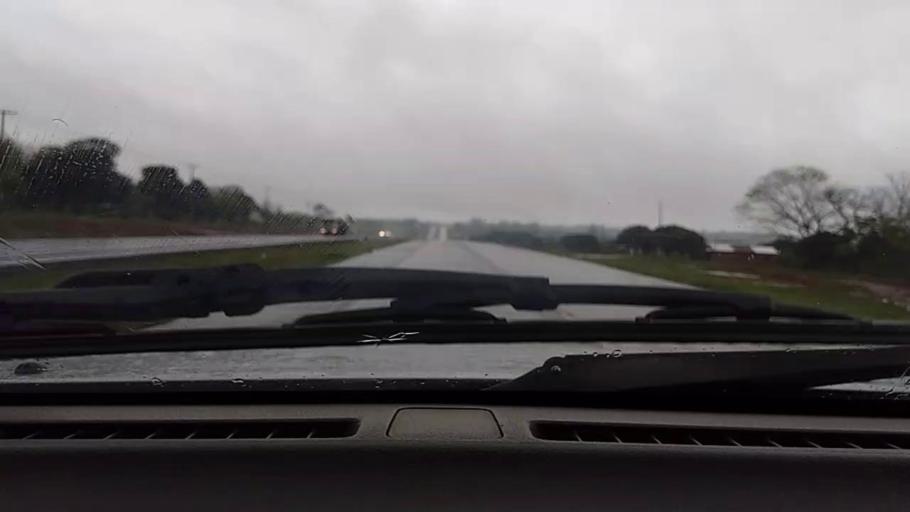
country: PY
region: Caaguazu
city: Repatriacion
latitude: -25.4660
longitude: -55.9486
